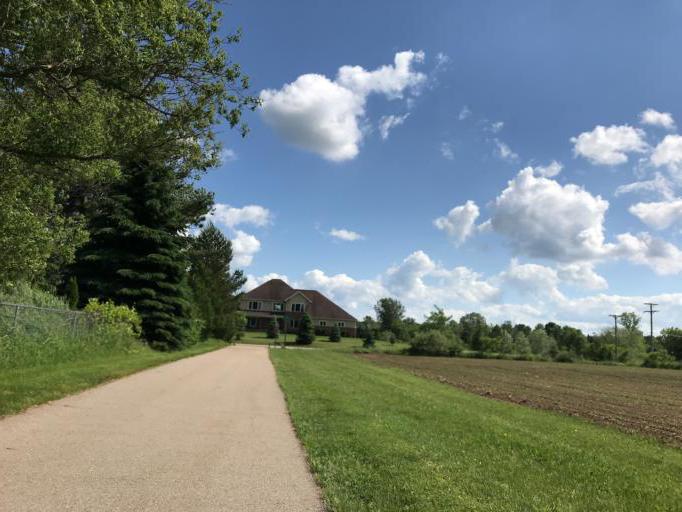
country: US
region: Michigan
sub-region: Oakland County
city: South Lyon
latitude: 42.4321
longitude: -83.6592
